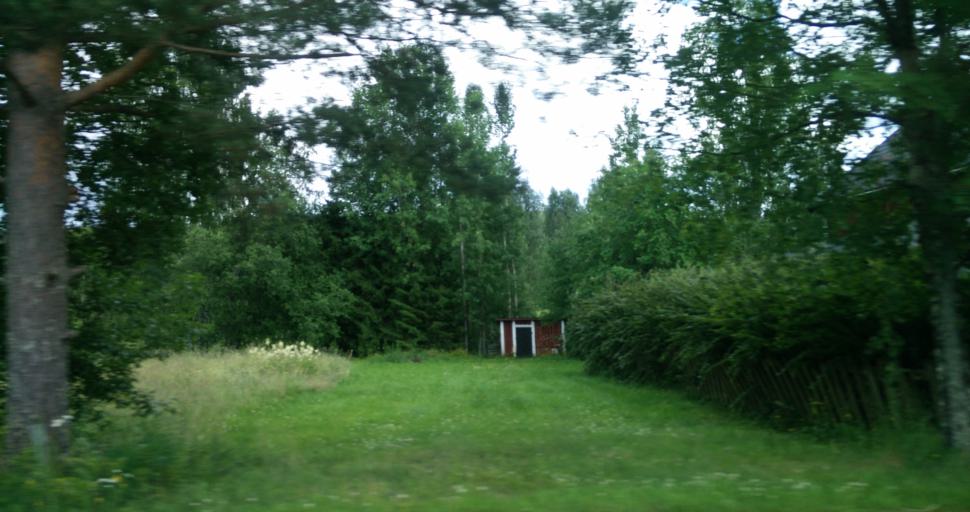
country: SE
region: Vaermland
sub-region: Hagfors Kommun
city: Hagfors
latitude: 60.0331
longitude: 13.6269
